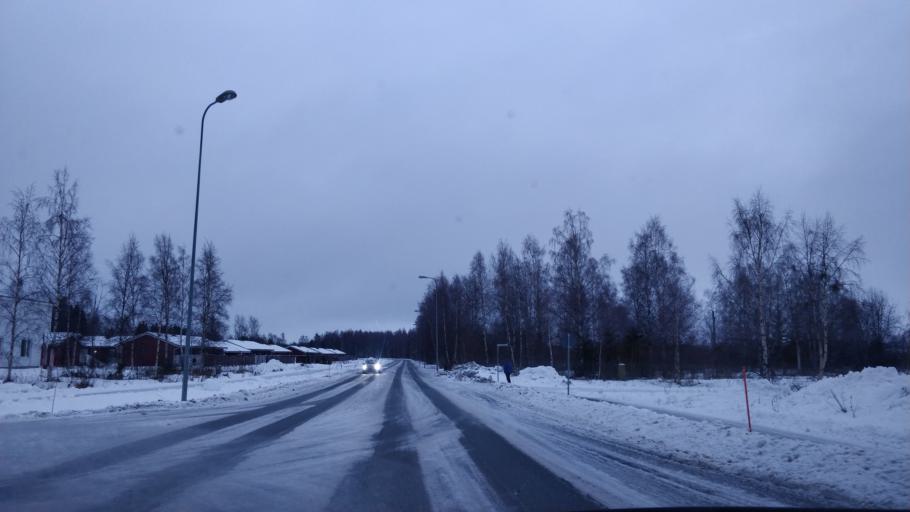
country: FI
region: Lapland
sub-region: Kemi-Tornio
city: Kemi
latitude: 65.7418
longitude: 24.5900
